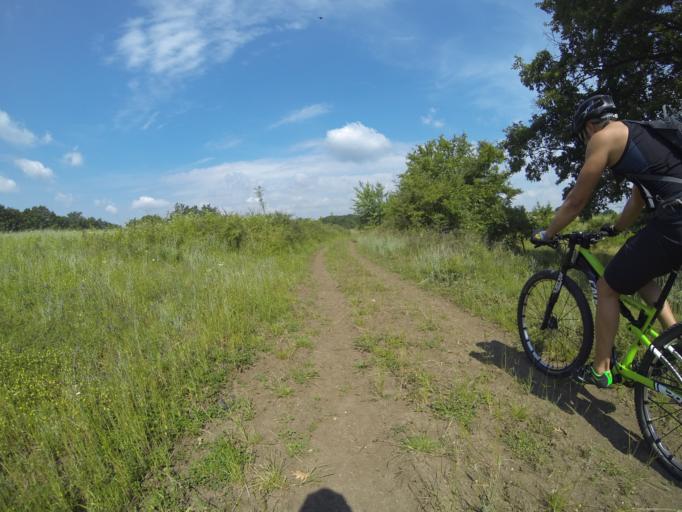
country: RO
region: Gorj
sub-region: Comuna Stoina
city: Stoina
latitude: 44.6330
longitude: 23.6076
